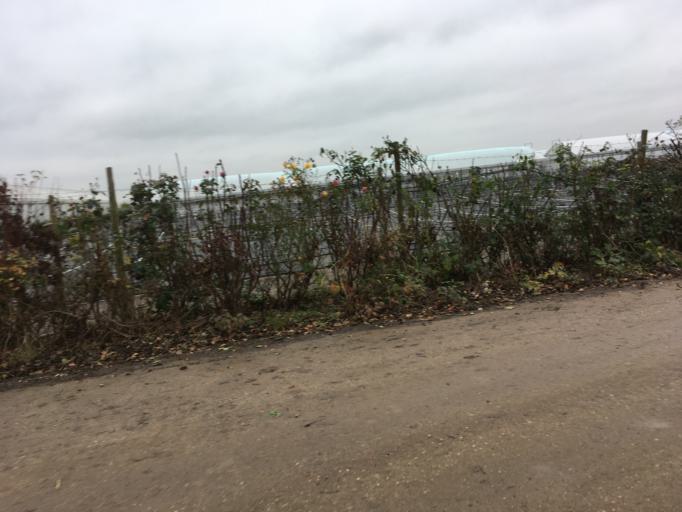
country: DE
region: Baden-Wuerttemberg
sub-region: Regierungsbezirk Stuttgart
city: Heilbronn
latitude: 49.1557
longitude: 9.1851
